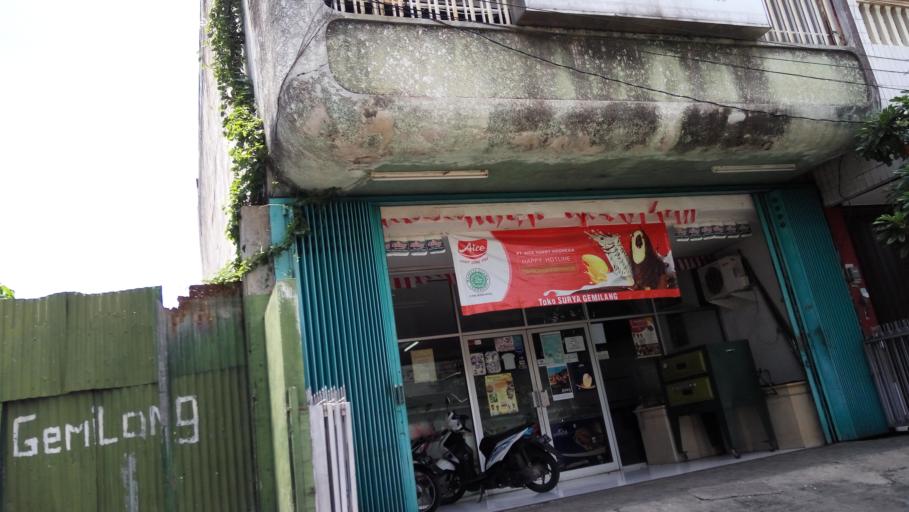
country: ID
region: East Java
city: Malang
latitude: -7.9865
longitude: 112.6279
